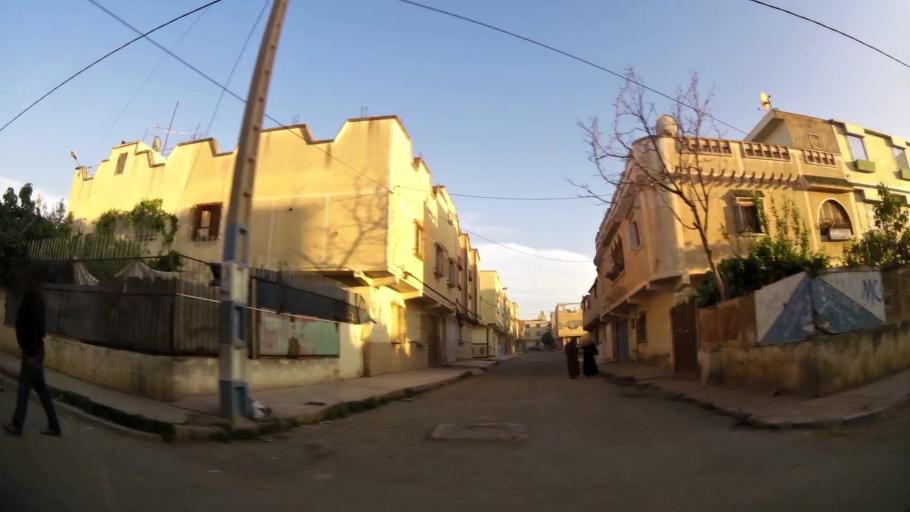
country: MA
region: Oriental
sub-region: Oujda-Angad
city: Oujda
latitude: 34.7094
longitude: -1.9126
